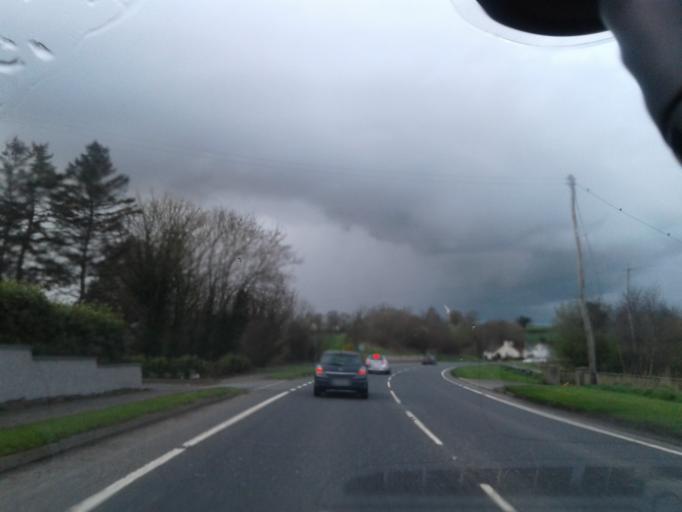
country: GB
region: Northern Ireland
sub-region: Strabane District
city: Sion Mills
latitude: 54.7663
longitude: -7.4686
